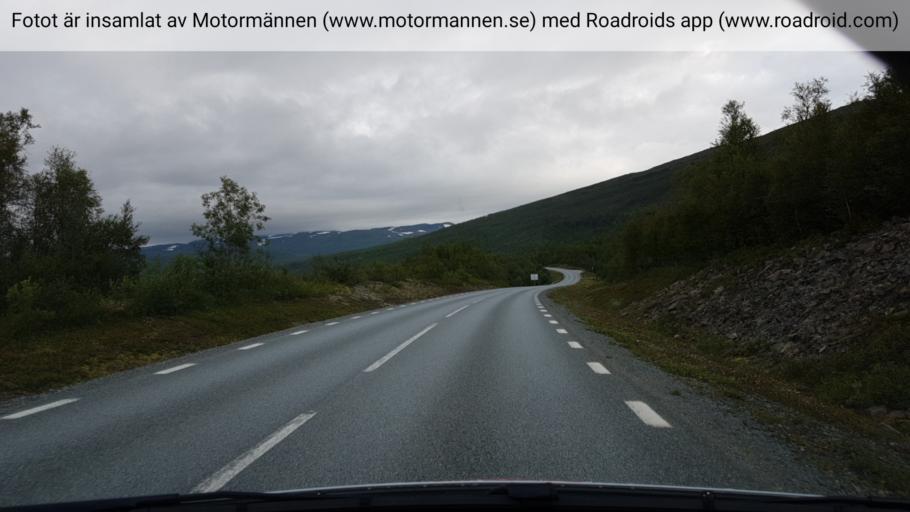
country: NO
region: Nordland
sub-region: Rana
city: Mo i Rana
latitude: 66.0634
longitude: 14.8724
